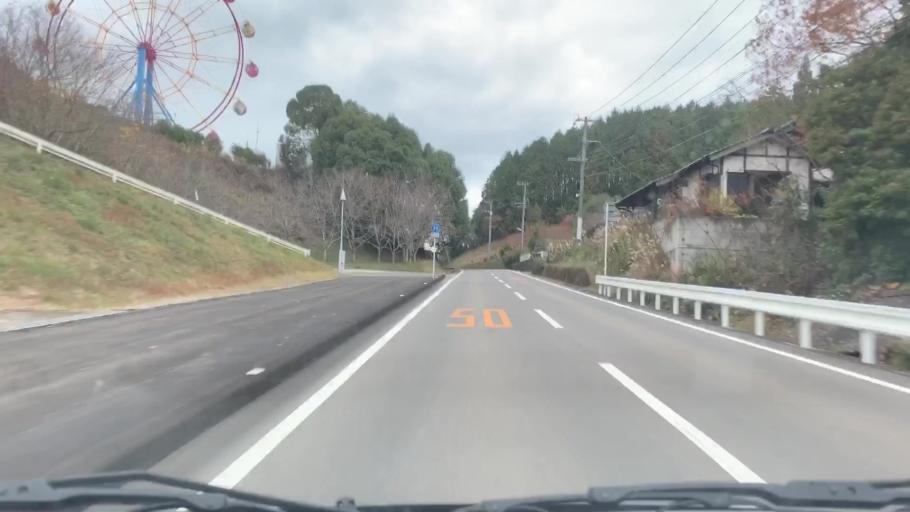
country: JP
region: Saga Prefecture
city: Ureshinomachi-shimojuku
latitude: 33.1299
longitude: 129.9774
